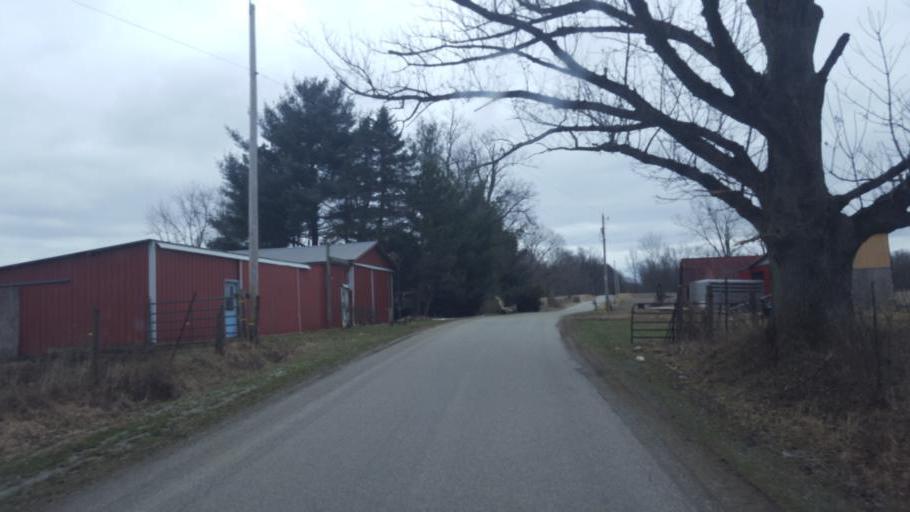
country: US
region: Ohio
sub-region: Crawford County
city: Galion
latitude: 40.6644
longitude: -82.7033
